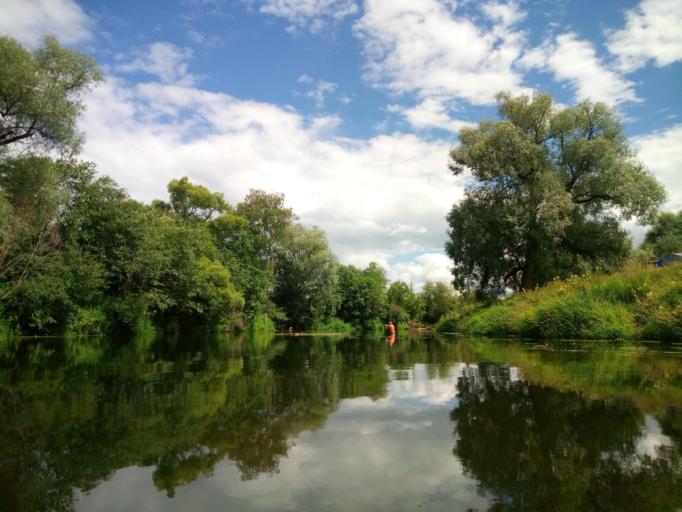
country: RU
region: Kaluga
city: Borovsk
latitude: 55.2118
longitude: 36.3706
